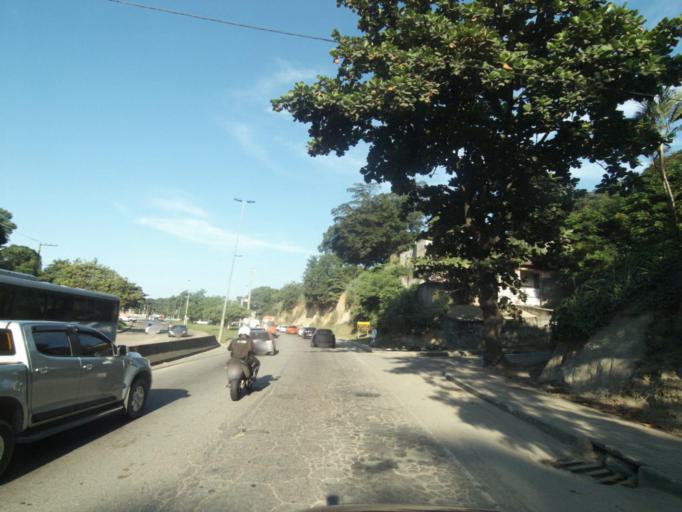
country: BR
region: Rio de Janeiro
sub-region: Niteroi
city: Niteroi
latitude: -22.8832
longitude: -43.0695
